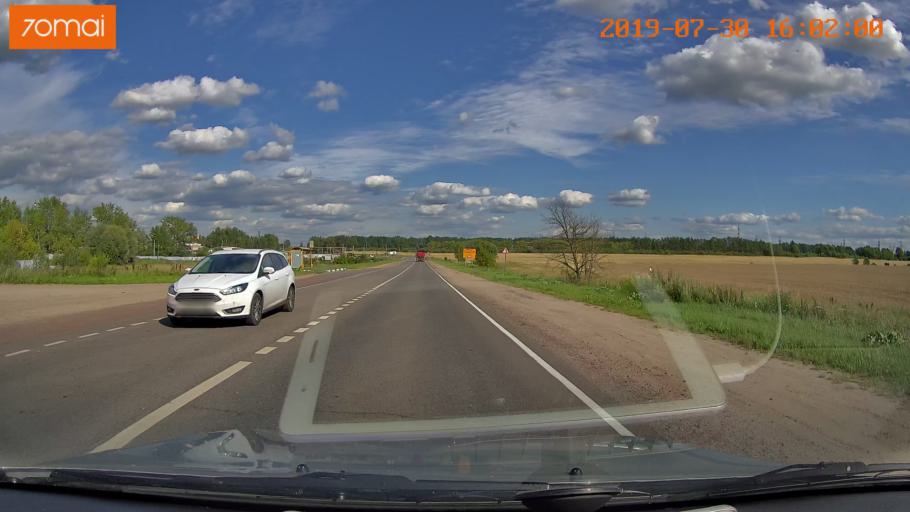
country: RU
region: Moskovskaya
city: Voskresensk
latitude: 55.2884
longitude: 38.6816
